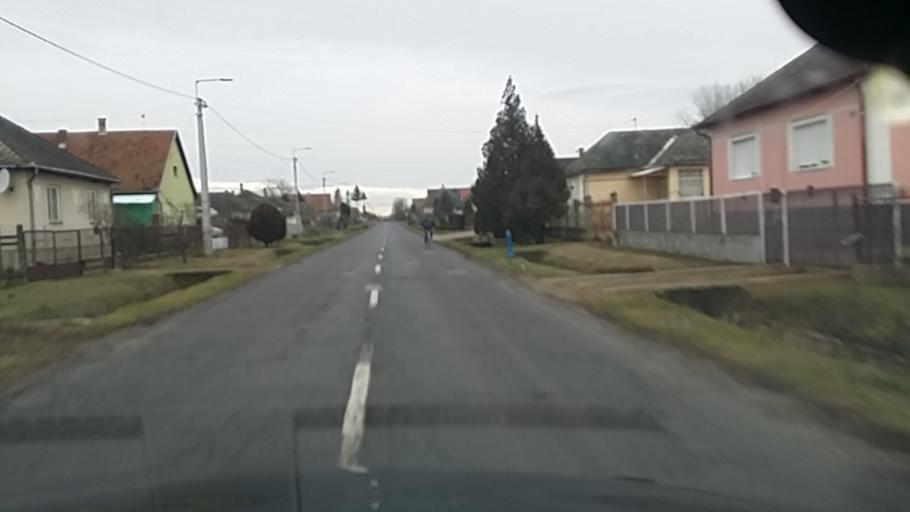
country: HU
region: Szabolcs-Szatmar-Bereg
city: Kek
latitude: 48.1003
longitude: 21.8827
